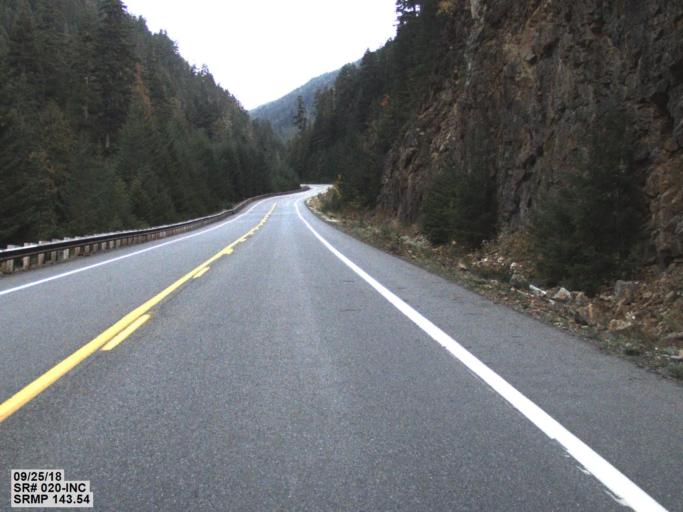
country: US
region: Washington
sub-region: Snohomish County
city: Darrington
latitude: 48.6844
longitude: -120.8846
